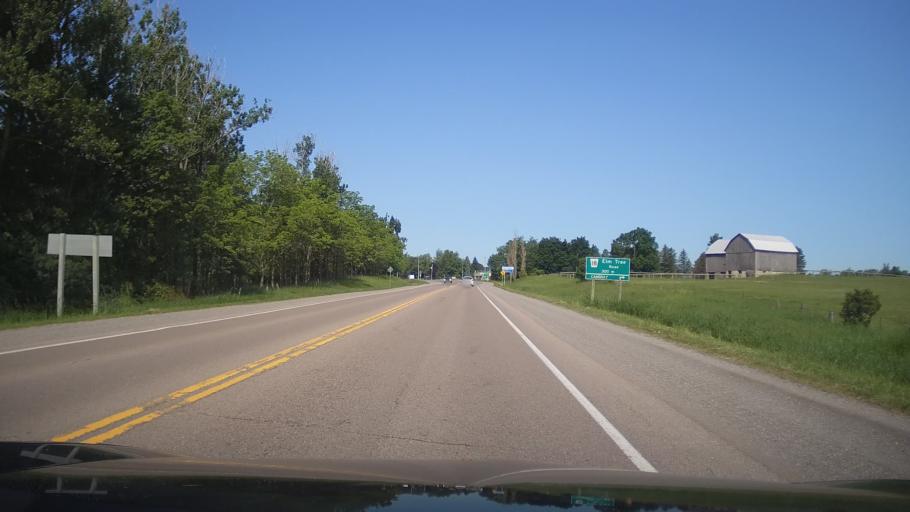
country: CA
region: Ontario
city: Omemee
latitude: 44.3475
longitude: -78.8002
